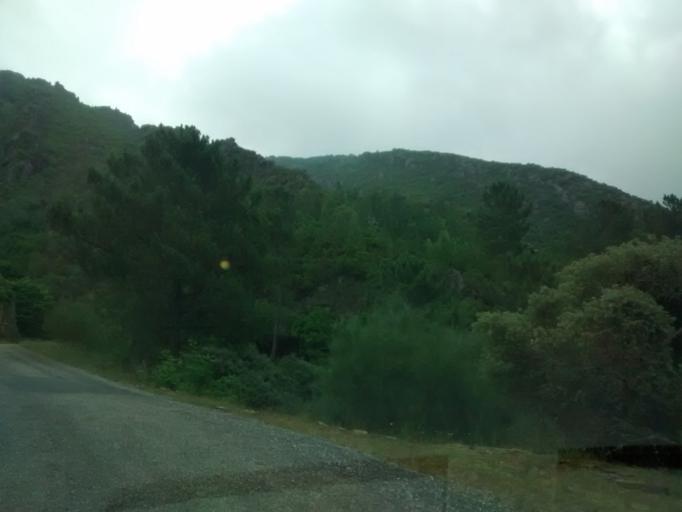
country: ES
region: Galicia
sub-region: Provincia de Ourense
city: Castro Caldelas
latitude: 42.4205
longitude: -7.3867
